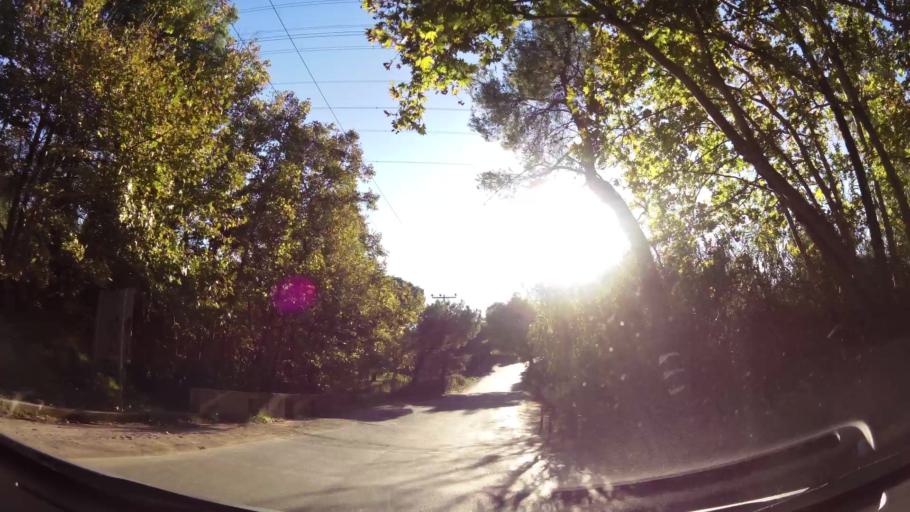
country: GR
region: Attica
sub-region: Nomarchia Anatolikis Attikis
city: Anoixi
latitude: 38.1273
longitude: 23.8453
